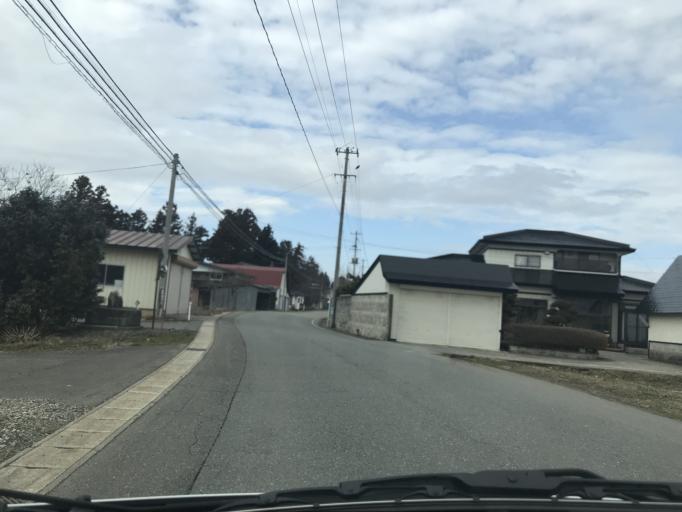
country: JP
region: Iwate
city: Kitakami
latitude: 39.3246
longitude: 140.9857
